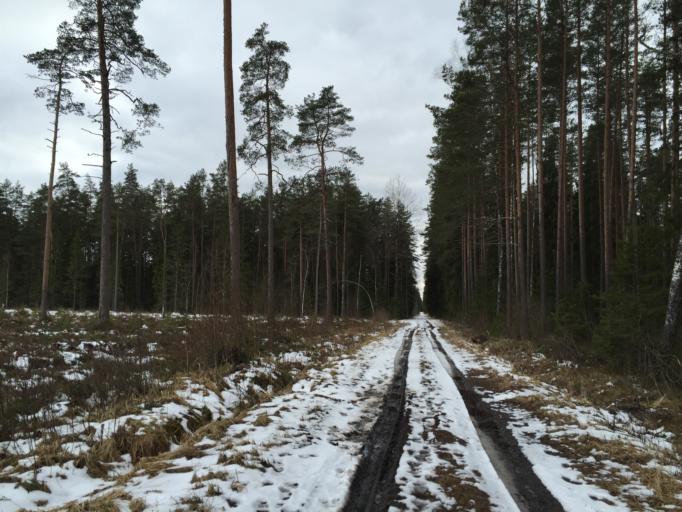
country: LV
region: Garkalne
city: Garkalne
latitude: 56.9605
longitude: 24.4785
